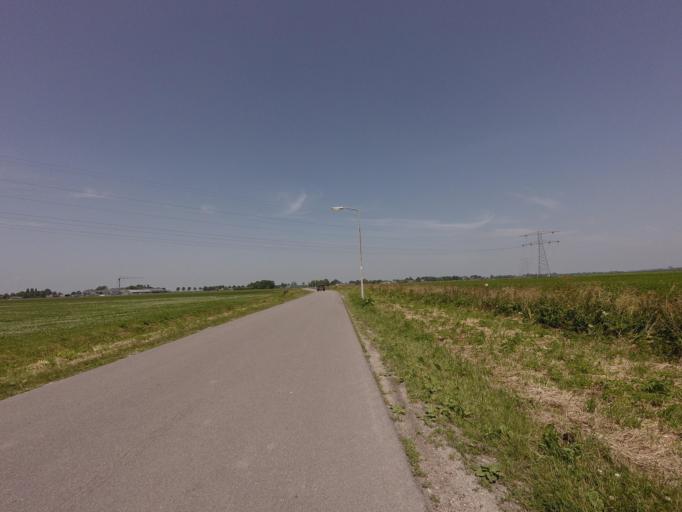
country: NL
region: North Holland
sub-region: Gemeente Opmeer
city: Opmeer
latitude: 52.6419
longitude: 4.9573
